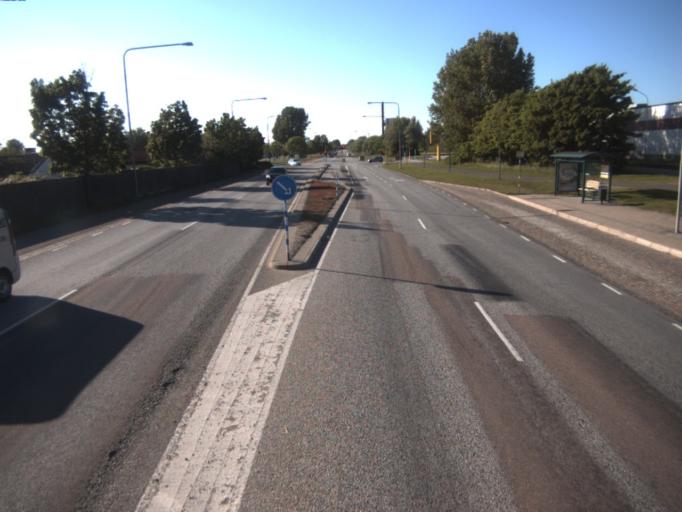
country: SE
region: Skane
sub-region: Helsingborg
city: Rydeback
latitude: 56.0043
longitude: 12.7395
